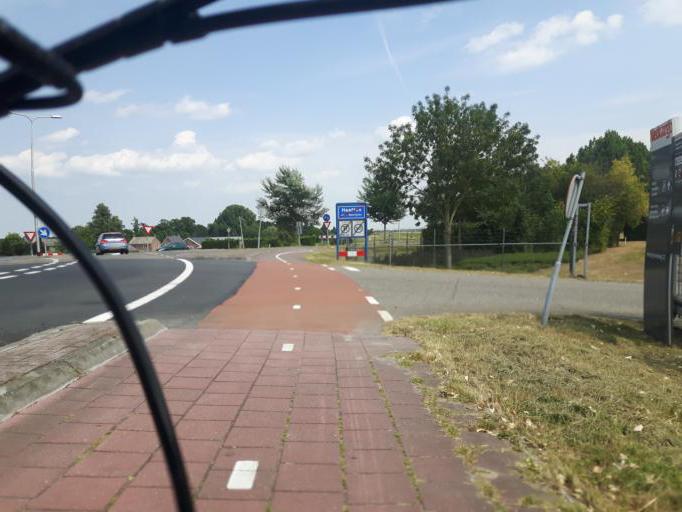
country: NL
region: Gelderland
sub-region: Gemeente Zaltbommel
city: Zaltbommel
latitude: 51.8205
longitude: 5.2255
